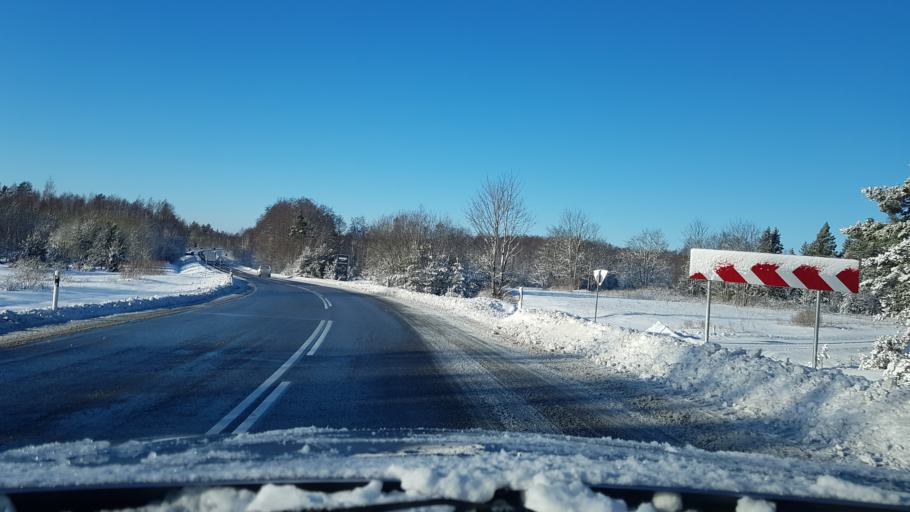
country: EE
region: Hiiumaa
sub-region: Kaerdla linn
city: Kardla
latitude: 58.9896
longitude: 22.7872
